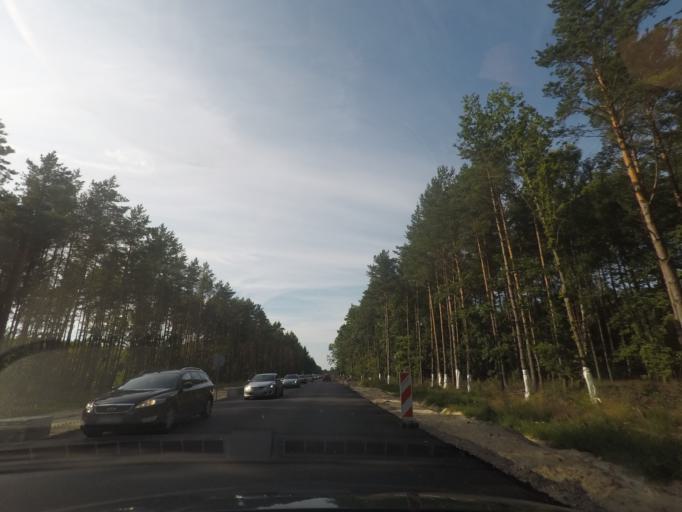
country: PL
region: Pomeranian Voivodeship
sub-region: Powiat leborski
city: Leba
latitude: 54.7160
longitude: 17.5763
